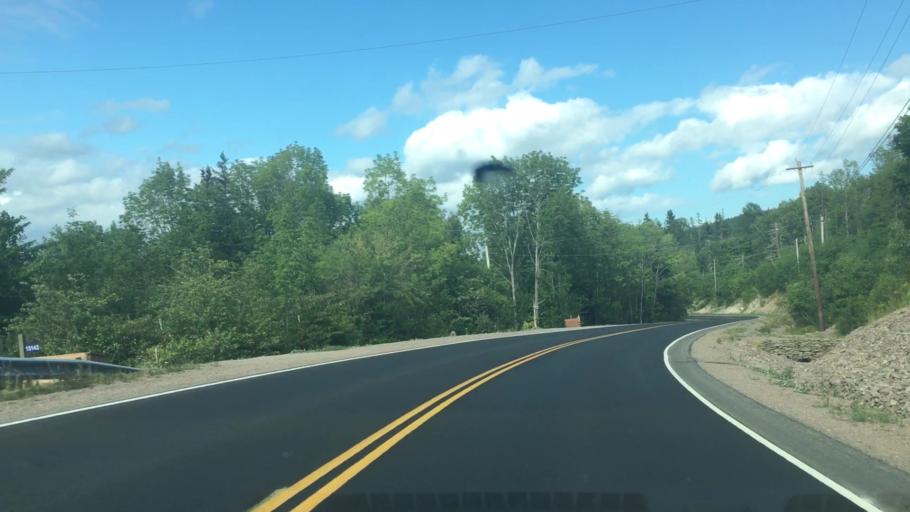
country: CA
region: Nova Scotia
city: Princeville
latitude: 45.7911
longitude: -60.7396
